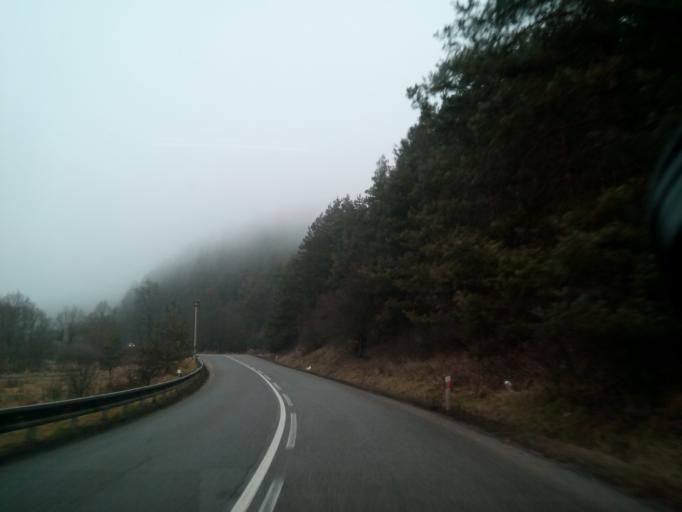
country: SK
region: Kosicky
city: Krompachy
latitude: 48.9324
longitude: 20.8405
